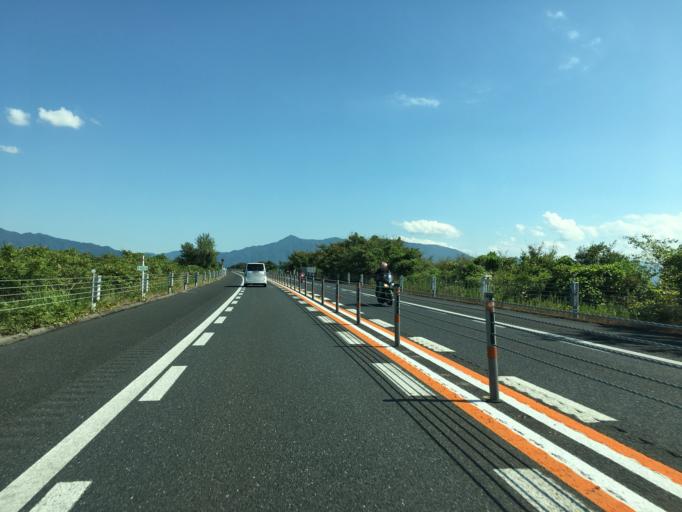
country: JP
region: Niigata
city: Niitsu-honcho
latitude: 37.7847
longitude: 139.1651
